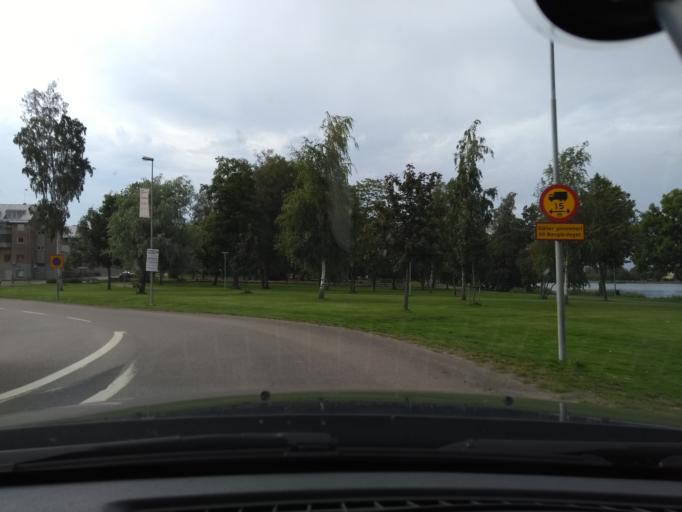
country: SE
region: Joenkoeping
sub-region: Nassjo Kommun
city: Nassjo
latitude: 57.6512
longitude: 14.7025
